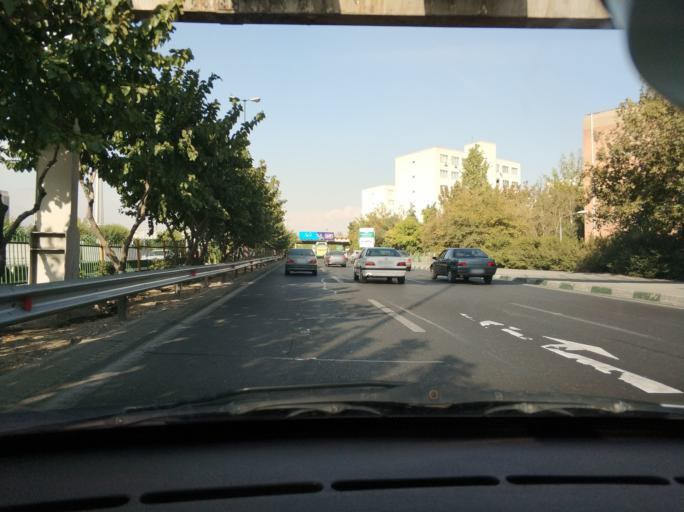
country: IR
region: Tehran
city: Tehran
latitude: 35.7274
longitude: 51.3672
